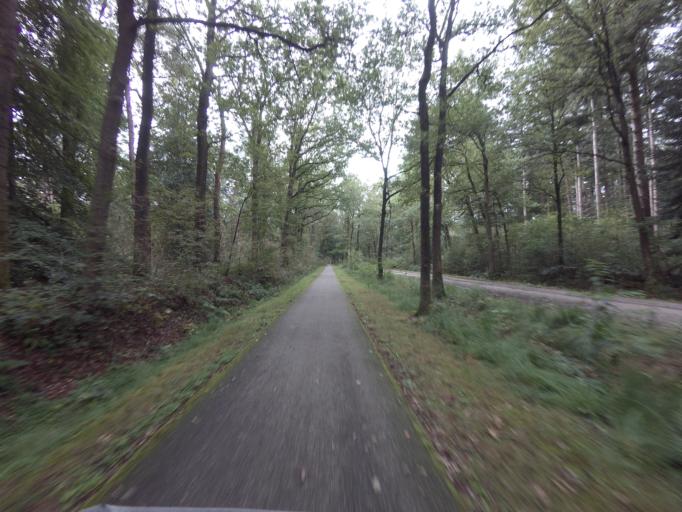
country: NL
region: Drenthe
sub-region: Gemeente Tynaarlo
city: Vries
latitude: 53.0775
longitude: 6.4658
